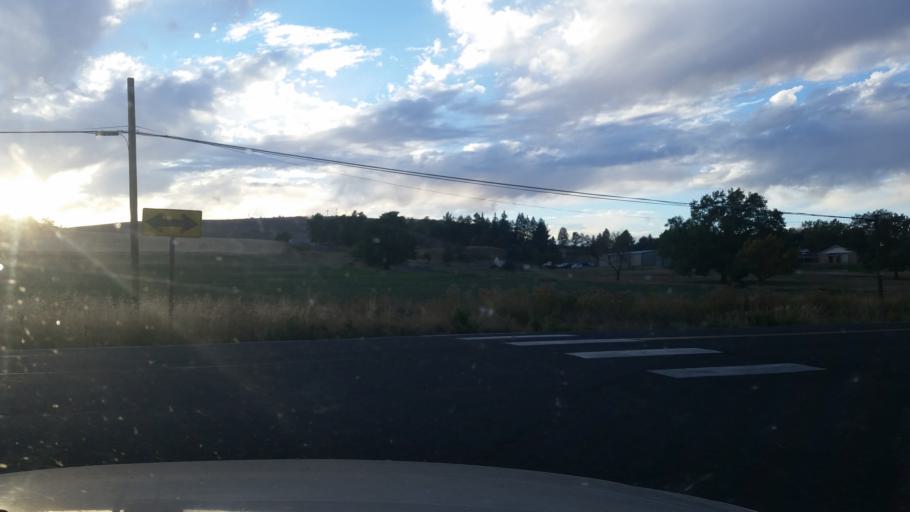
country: US
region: Washington
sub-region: Spokane County
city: Medical Lake
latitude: 47.5476
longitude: -117.7043
